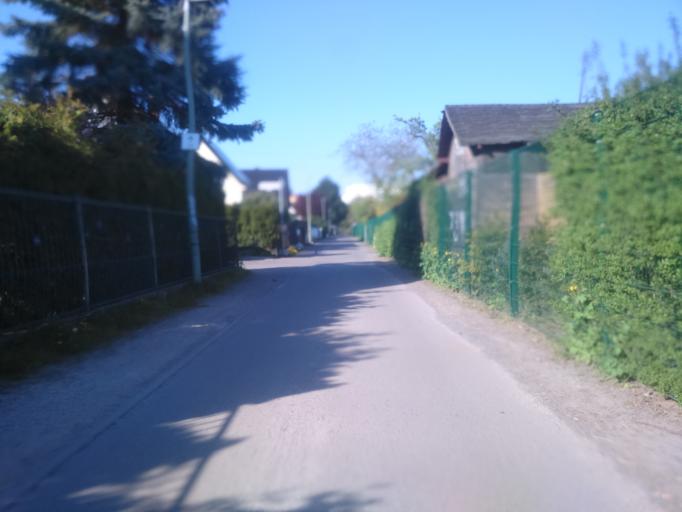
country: DE
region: Berlin
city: Neu-Hohenschoenhausen
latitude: 52.5576
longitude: 13.5073
